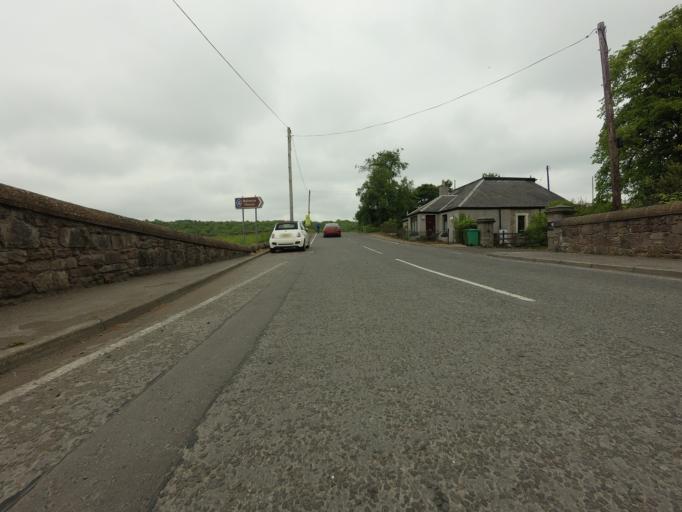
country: GB
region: Scotland
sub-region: Fife
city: Townhill
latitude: 56.1069
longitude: -3.4549
